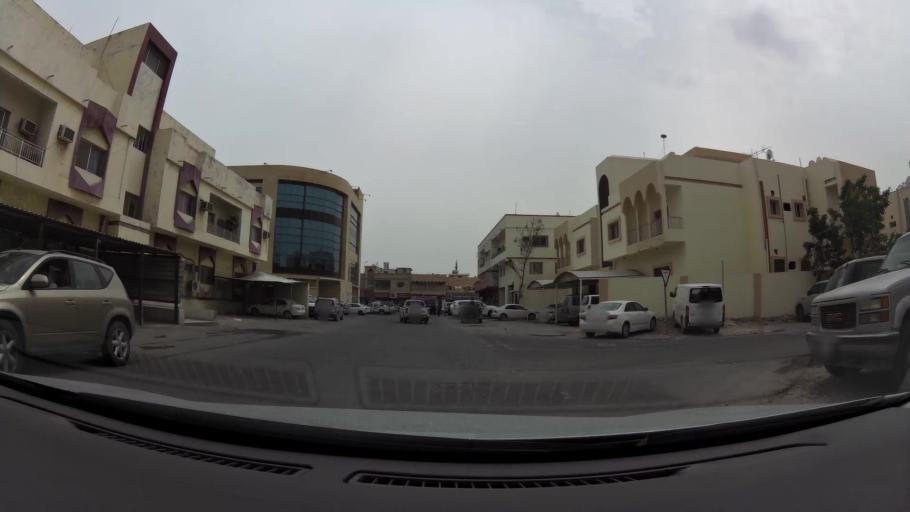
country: QA
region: Baladiyat ad Dawhah
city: Doha
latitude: 25.2513
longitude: 51.5515
